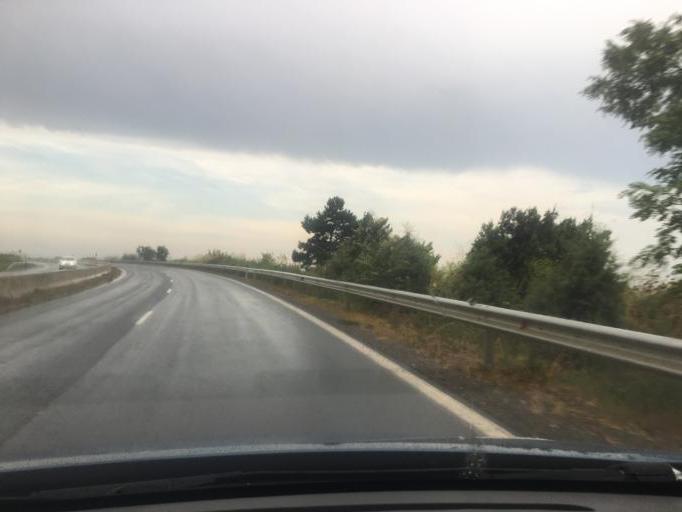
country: BG
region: Burgas
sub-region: Obshtina Pomorie
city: Pomorie
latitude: 42.5595
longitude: 27.5516
